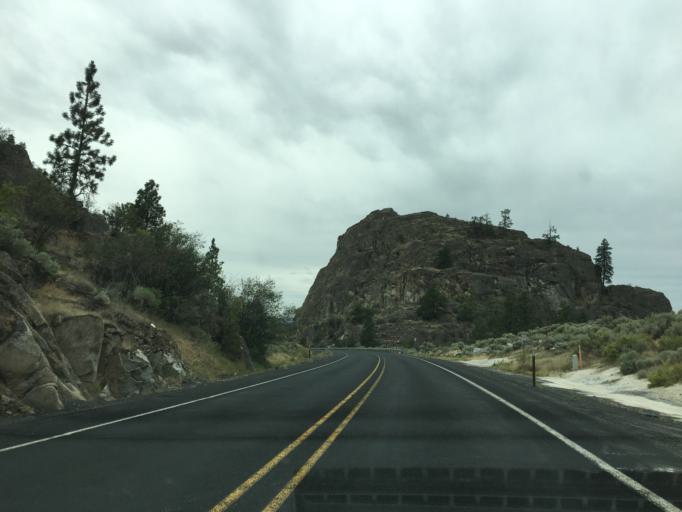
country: US
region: Washington
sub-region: Okanogan County
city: Coulee Dam
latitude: 47.8854
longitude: -119.0875
